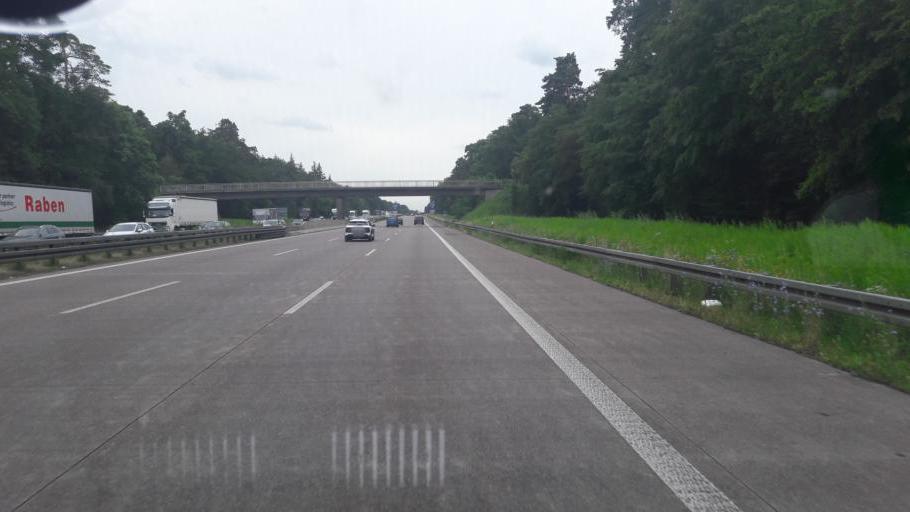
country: DE
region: Baden-Wuerttemberg
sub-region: Karlsruhe Region
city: Kronau
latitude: 49.2111
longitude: 8.5996
